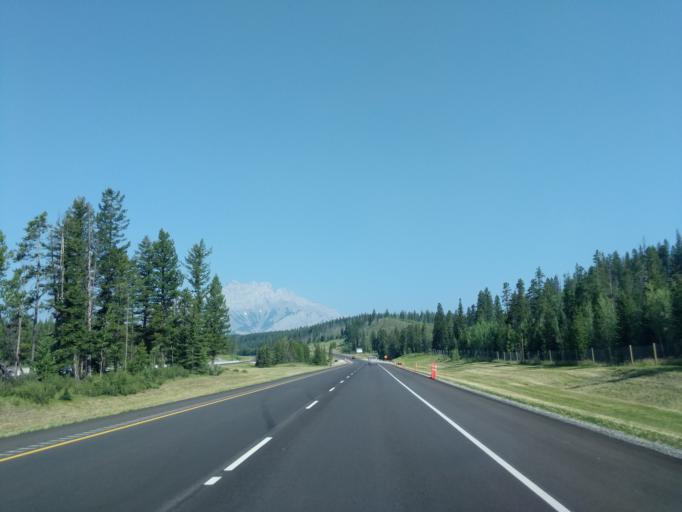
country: CA
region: Alberta
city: Canmore
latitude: 51.1597
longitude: -115.4383
